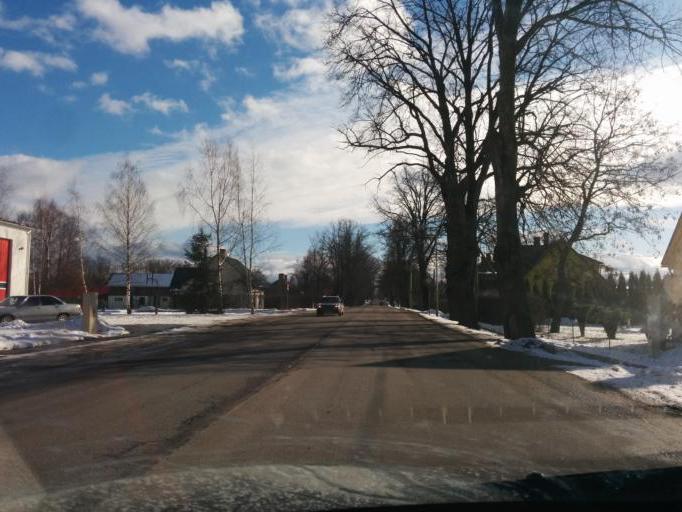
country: LV
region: Gulbenes Rajons
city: Gulbene
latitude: 57.1680
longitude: 26.7531
